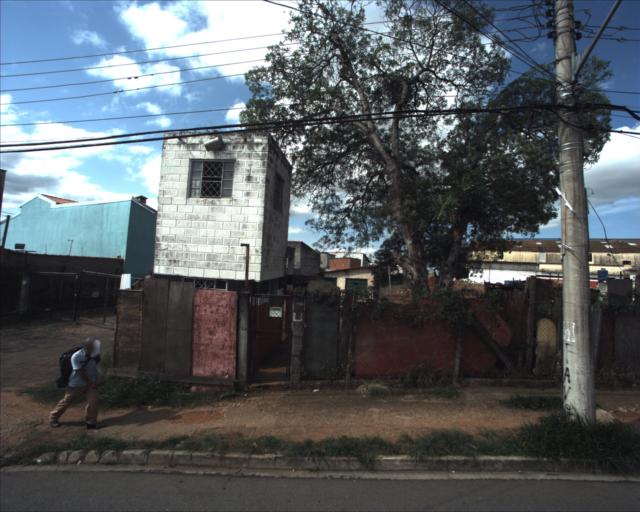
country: BR
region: Sao Paulo
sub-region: Sorocaba
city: Sorocaba
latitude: -23.3965
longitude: -47.3789
